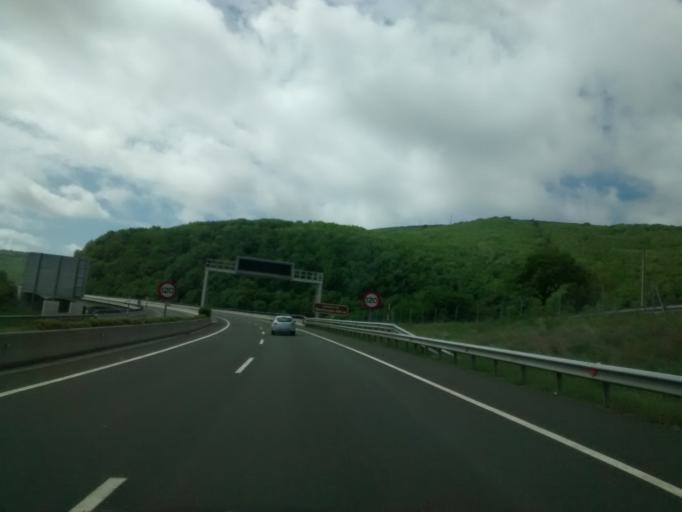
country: ES
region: Cantabria
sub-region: Provincia de Cantabria
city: Santiurde de Reinosa
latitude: 43.0614
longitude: -4.0906
